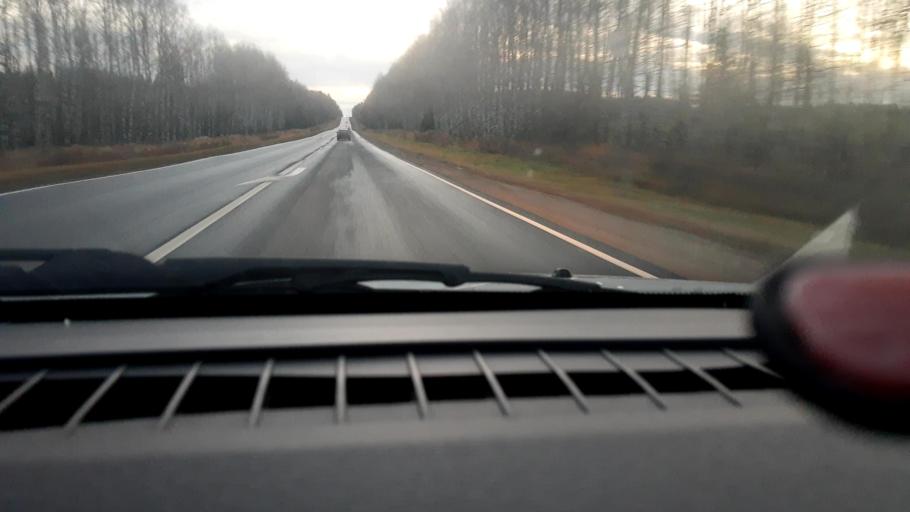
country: RU
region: Nizjnij Novgorod
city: Vladimirskoye
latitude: 56.9556
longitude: 45.0938
